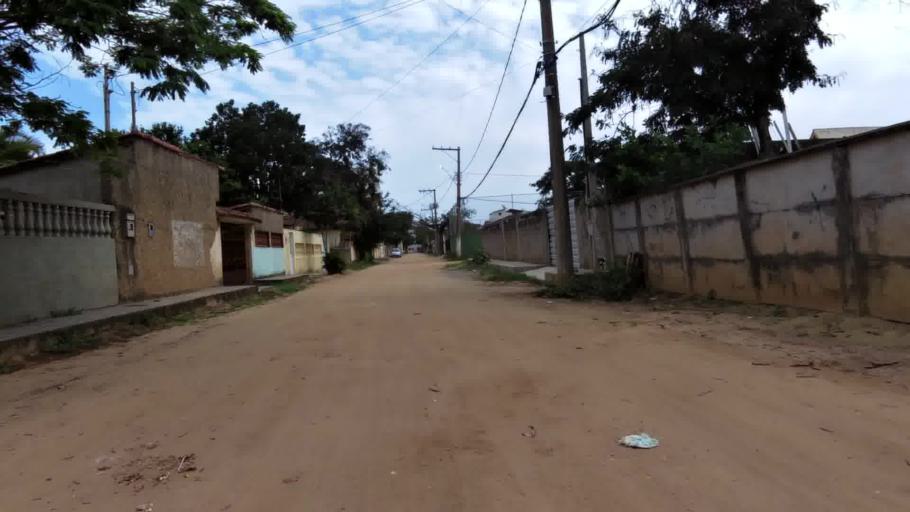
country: BR
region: Espirito Santo
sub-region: Piuma
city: Piuma
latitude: -20.8405
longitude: -40.7319
